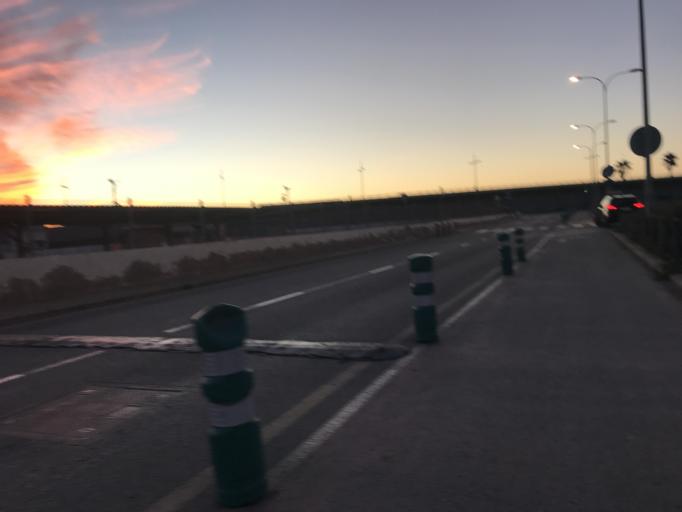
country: ES
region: Valencia
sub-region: Provincia de Alicante
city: Torrevieja
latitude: 37.9737
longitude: -0.6796
